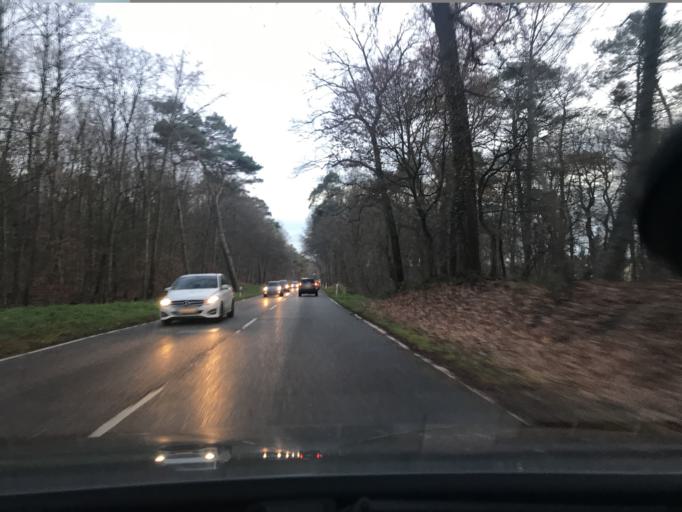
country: DE
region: North Rhine-Westphalia
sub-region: Regierungsbezirk Koln
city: Merheim
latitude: 50.9562
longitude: 7.0760
